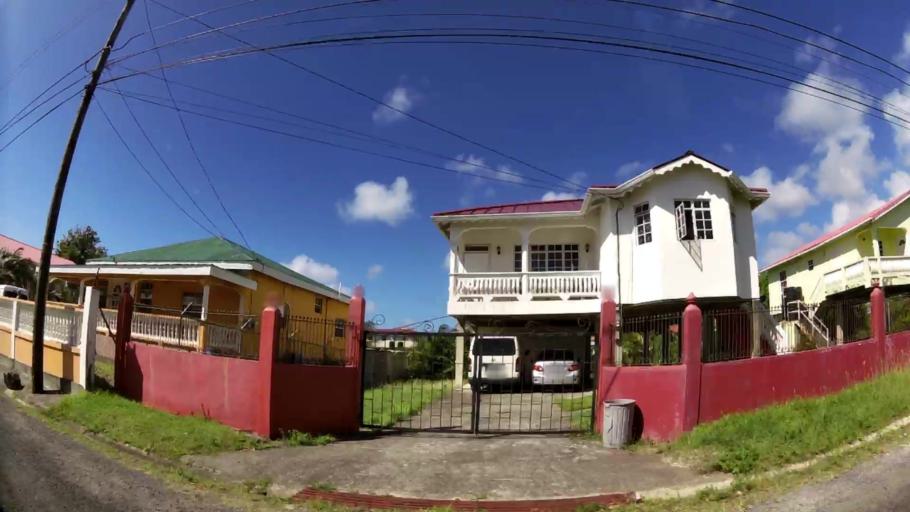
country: LC
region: Laborie Quarter
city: Laborie
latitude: 13.7458
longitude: -60.9731
